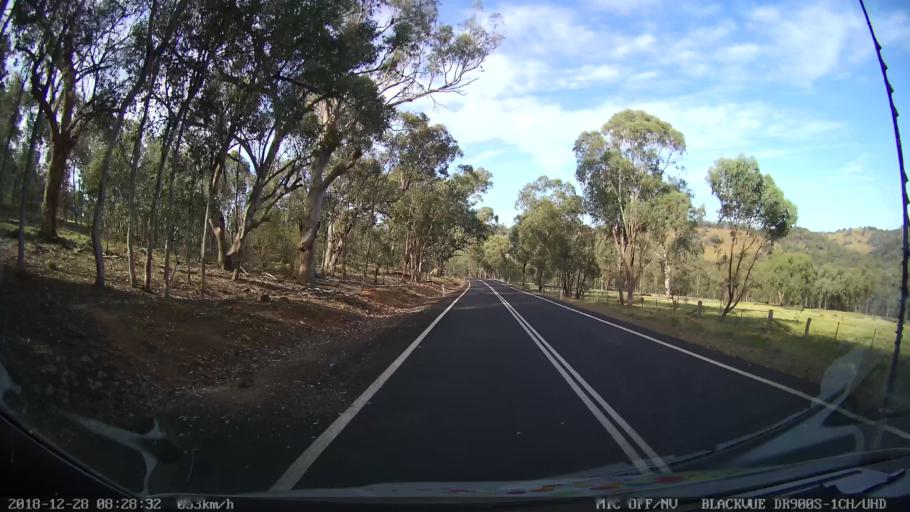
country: AU
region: New South Wales
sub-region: Blayney
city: Blayney
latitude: -33.9420
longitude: 149.3268
